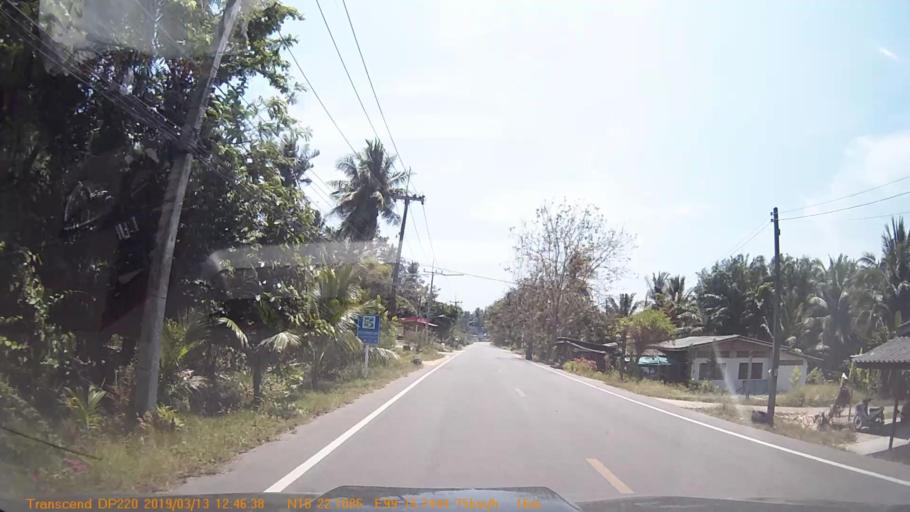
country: TH
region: Chumphon
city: Chumphon
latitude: 10.3680
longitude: 99.2624
